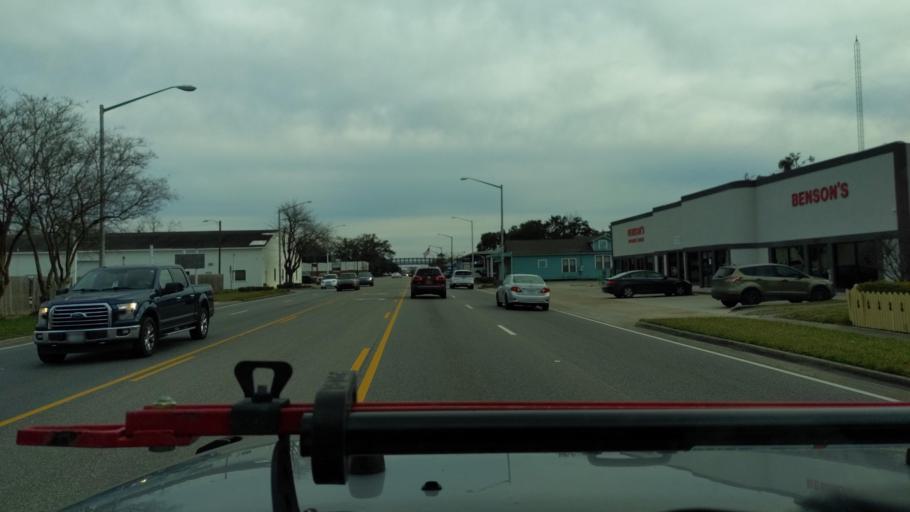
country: US
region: Alabama
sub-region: Baldwin County
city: Foley
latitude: 30.4114
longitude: -87.6839
